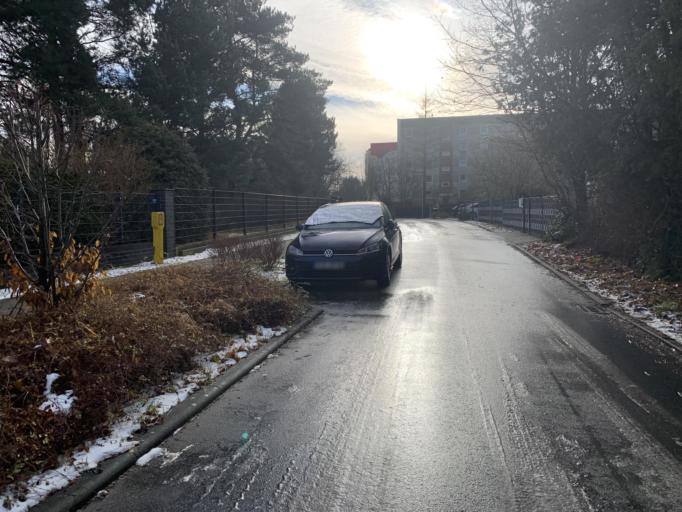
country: DE
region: Brandenburg
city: Oranienburg
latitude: 52.7441
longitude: 13.2469
